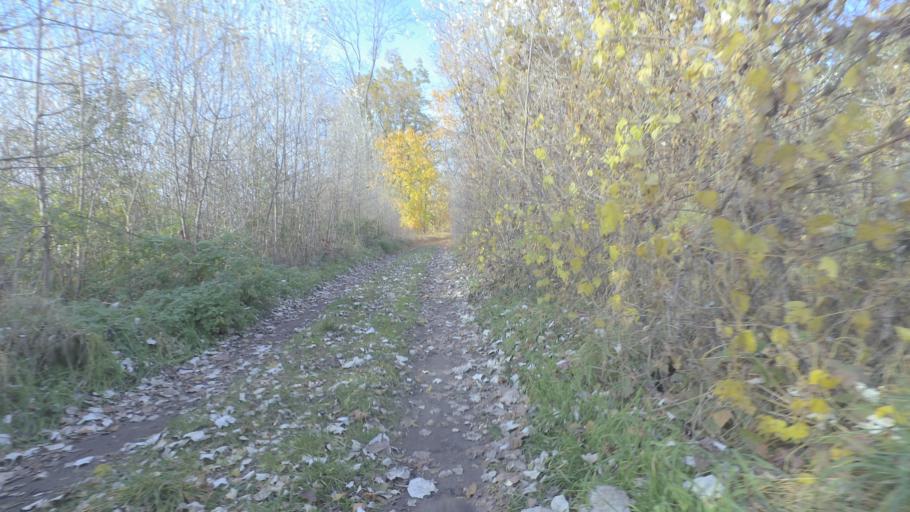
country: DE
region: Brandenburg
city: Trebbin
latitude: 52.2291
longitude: 13.2899
